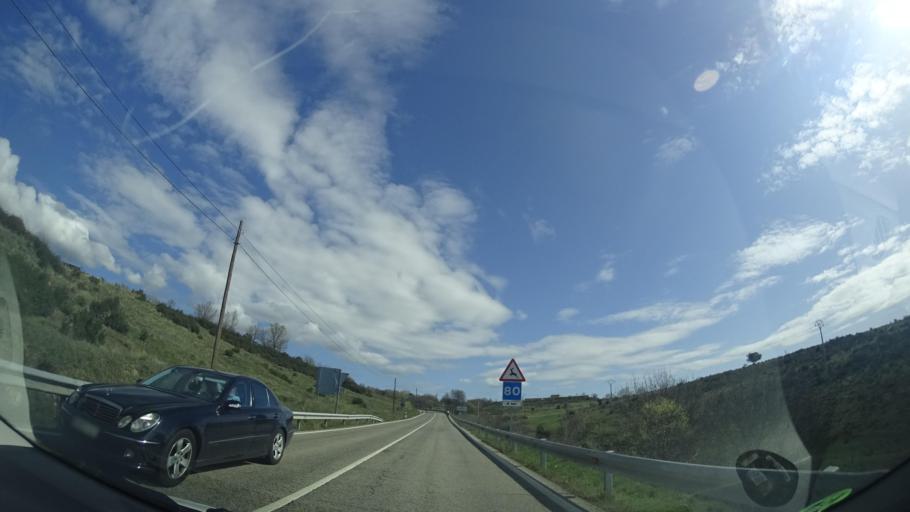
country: ES
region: Madrid
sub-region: Provincia de Madrid
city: Miraflores de la Sierra
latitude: 40.7713
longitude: -3.7799
